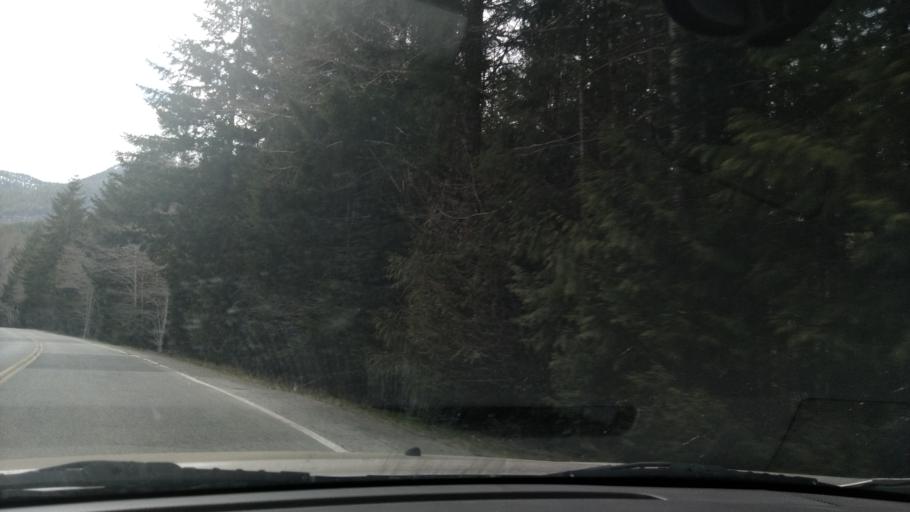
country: CA
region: British Columbia
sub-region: Regional District of Alberni-Clayoquot
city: Tofino
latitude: 49.8377
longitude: -125.9412
